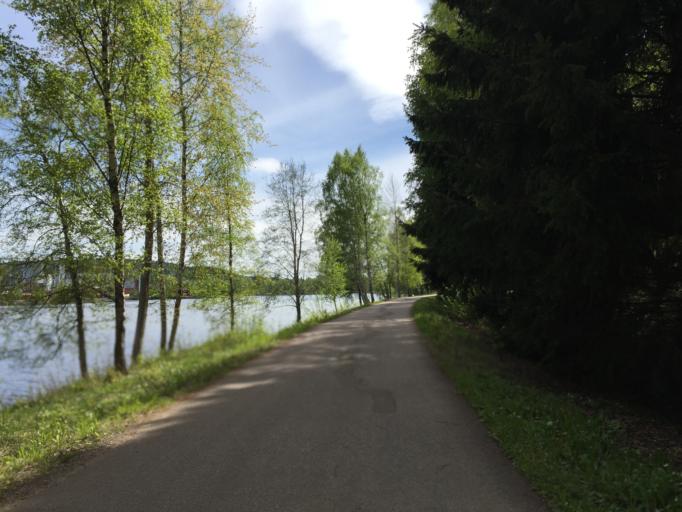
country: SE
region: Dalarna
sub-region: Ludvika Kommun
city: Ludvika
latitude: 60.1437
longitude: 15.1595
